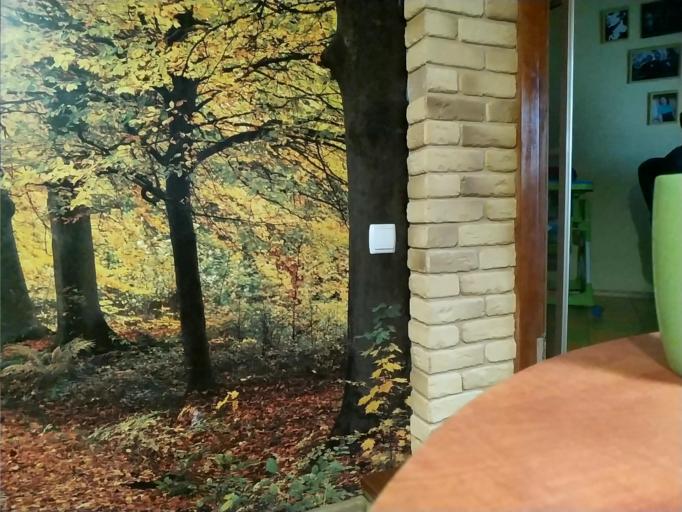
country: RU
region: Tverskaya
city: Staraya Toropa
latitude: 56.3429
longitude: 31.8436
